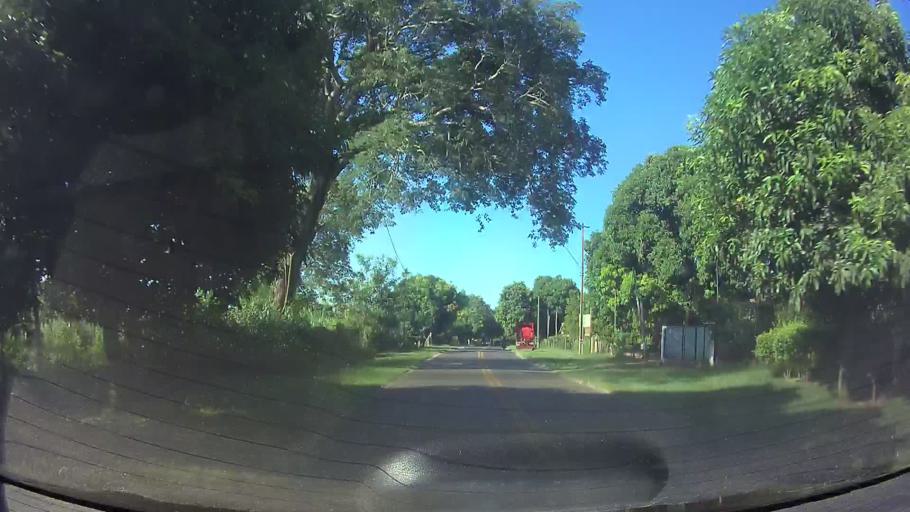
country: PY
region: Cordillera
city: Atyra
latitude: -25.2960
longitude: -57.1847
